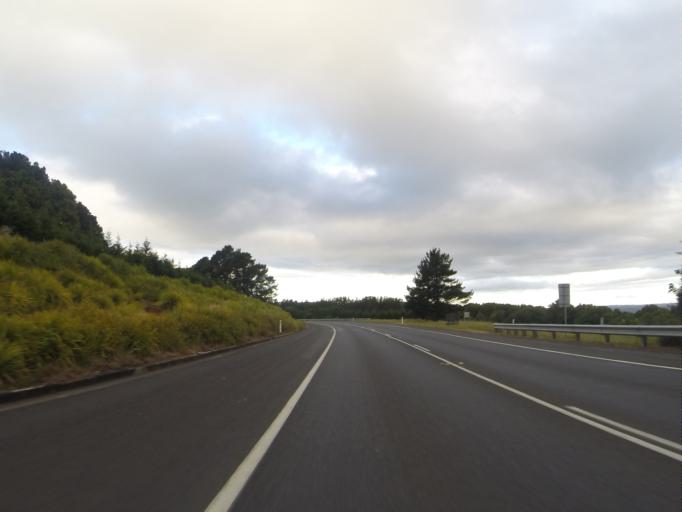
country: AU
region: New South Wales
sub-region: Shellharbour
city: Calderwood
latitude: -34.5876
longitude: 150.6150
